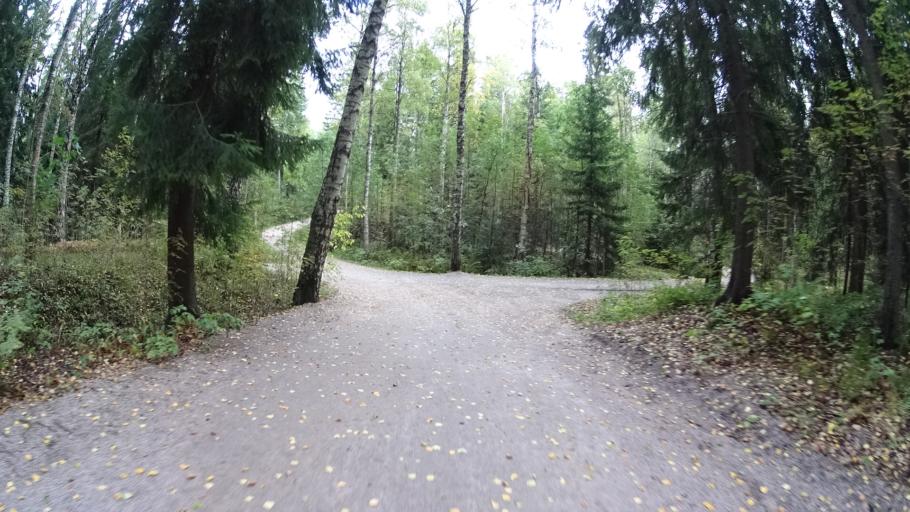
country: FI
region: Uusimaa
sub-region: Helsinki
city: Helsinki
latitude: 60.2351
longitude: 24.9060
